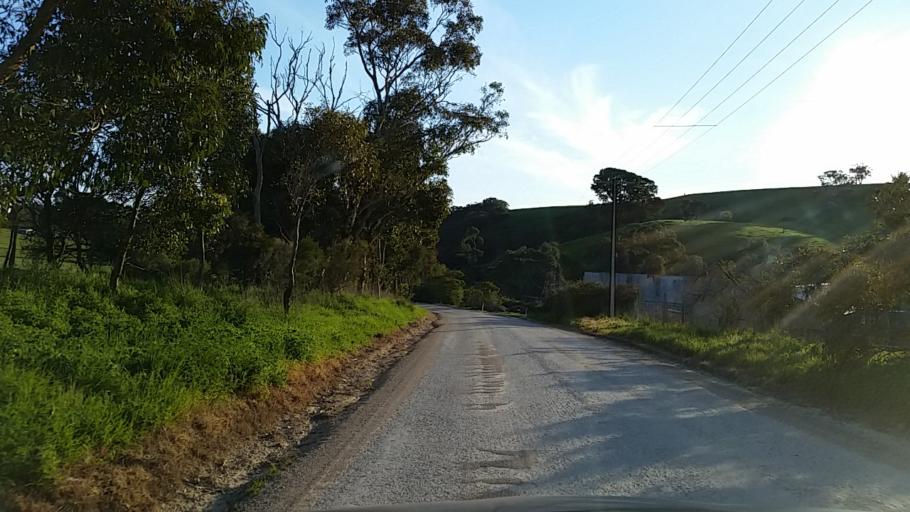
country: AU
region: South Australia
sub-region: Alexandrina
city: Mount Compass
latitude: -35.2858
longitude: 138.6934
